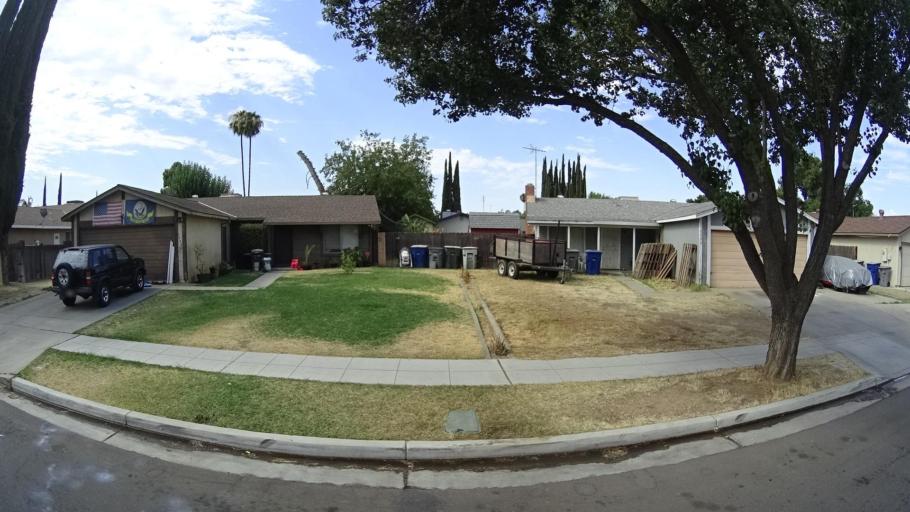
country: US
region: California
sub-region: Fresno County
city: Tarpey Village
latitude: 36.7866
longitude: -119.6846
